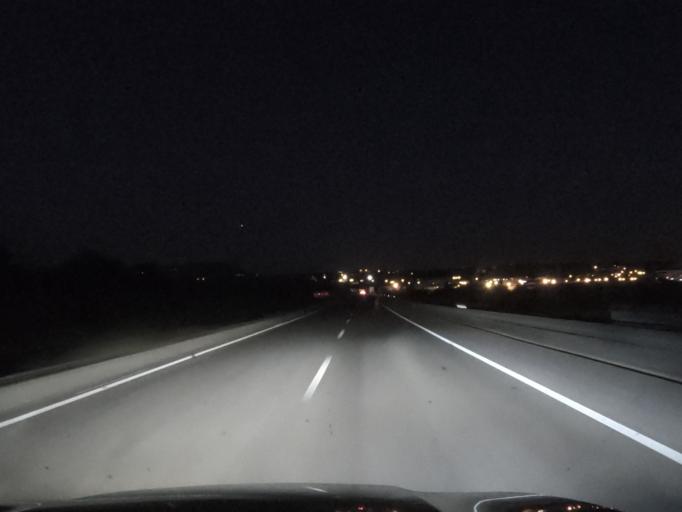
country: PT
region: Faro
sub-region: Loule
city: Loule
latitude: 37.1362
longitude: -8.0426
